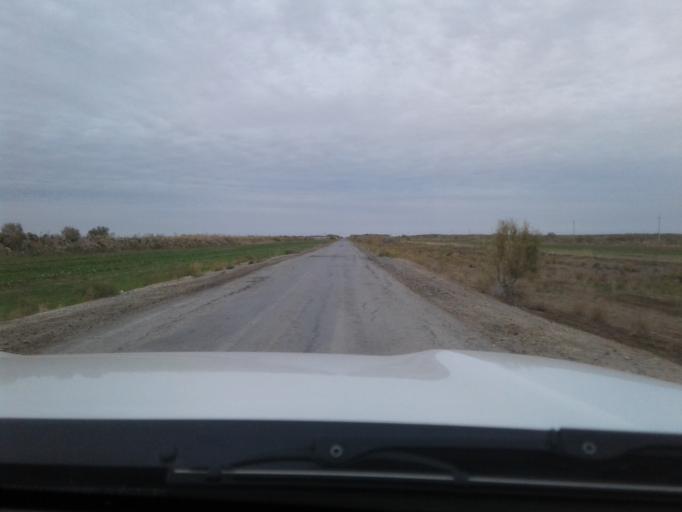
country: TM
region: Mary
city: Mary
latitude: 38.1977
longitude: 61.7529
